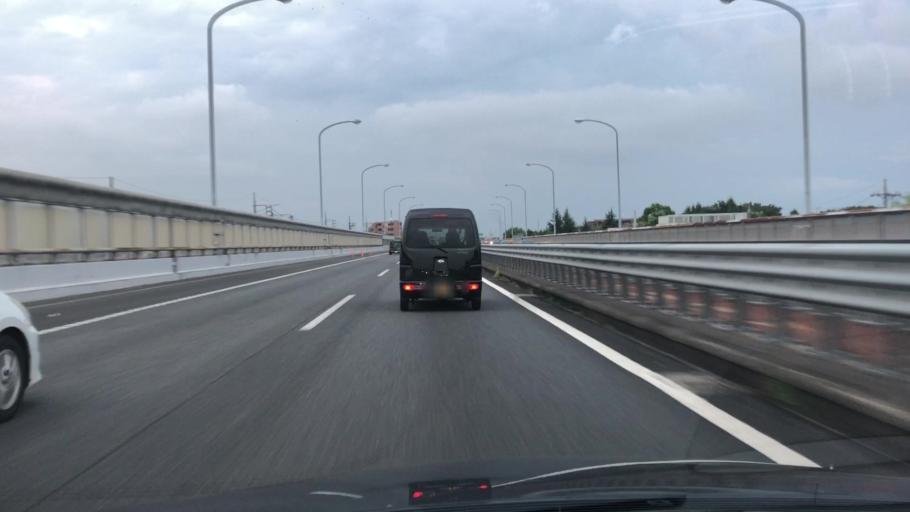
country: JP
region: Tokyo
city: Kokubunji
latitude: 35.6640
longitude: 139.4653
